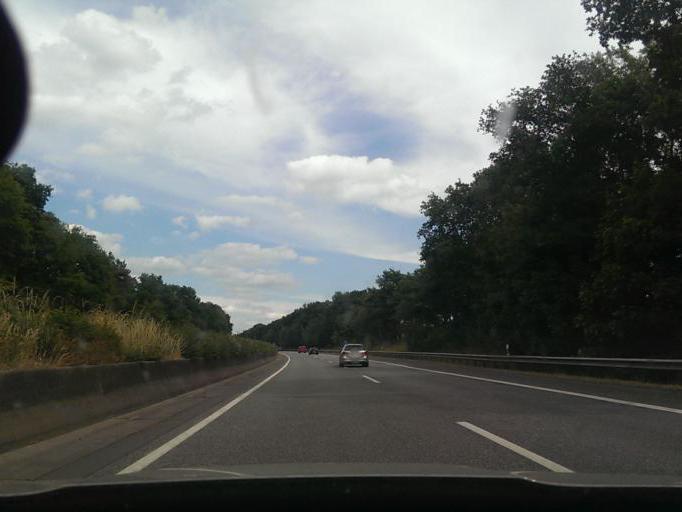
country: DE
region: Lower Saxony
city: Ahsen-Oetzen
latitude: 53.0144
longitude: 9.0854
